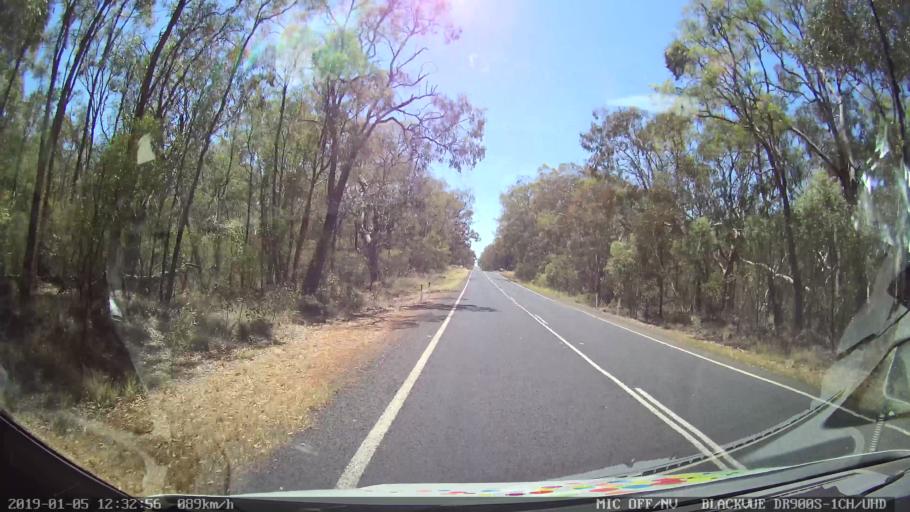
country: AU
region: New South Wales
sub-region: Warrumbungle Shire
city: Coonabarabran
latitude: -31.2159
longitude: 149.3870
